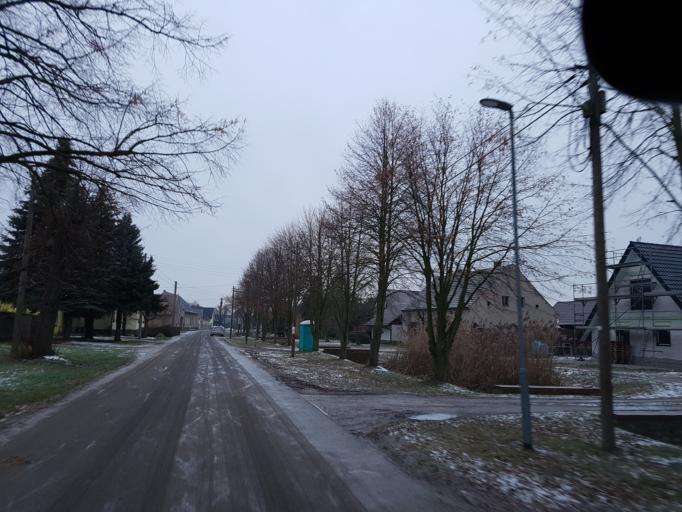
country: DE
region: Brandenburg
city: Ruckersdorf
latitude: 51.5752
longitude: 13.5623
